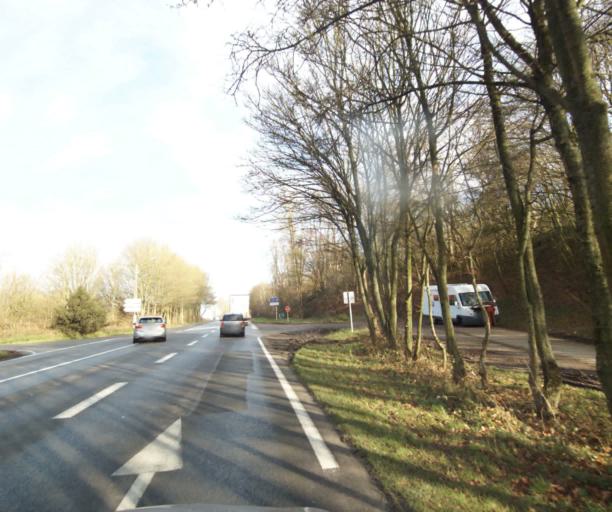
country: FR
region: Nord-Pas-de-Calais
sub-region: Departement du Nord
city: Famars
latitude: 50.3244
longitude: 3.5061
